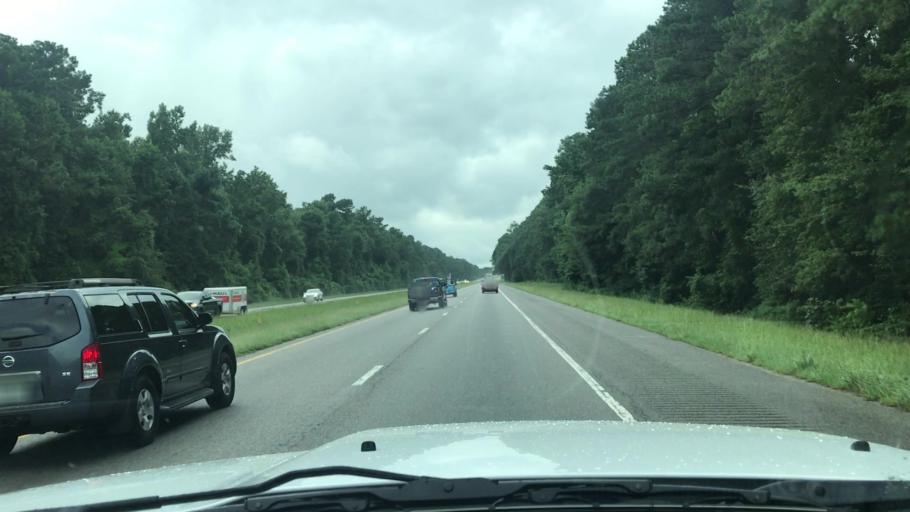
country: US
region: South Carolina
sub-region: Orangeburg County
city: Brookdale
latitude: 33.5097
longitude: -80.7798
